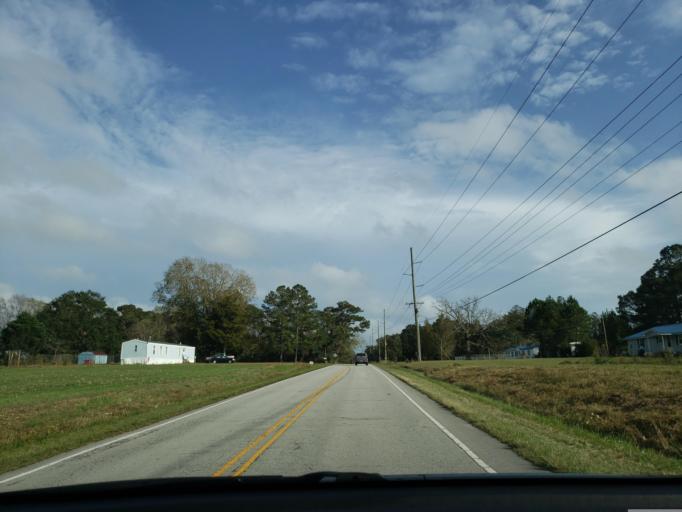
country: US
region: North Carolina
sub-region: Onslow County
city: Jacksonville
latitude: 34.6886
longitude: -77.5375
